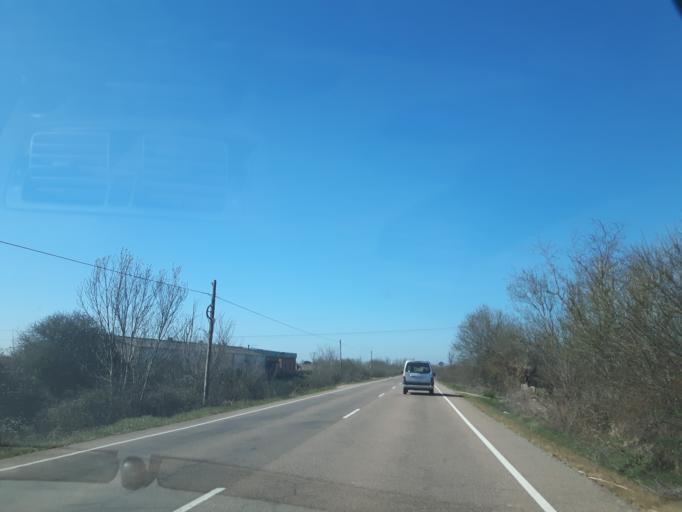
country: ES
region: Castille and Leon
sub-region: Provincia de Salamanca
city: Lumbrales
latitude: 40.9435
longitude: -6.6948
